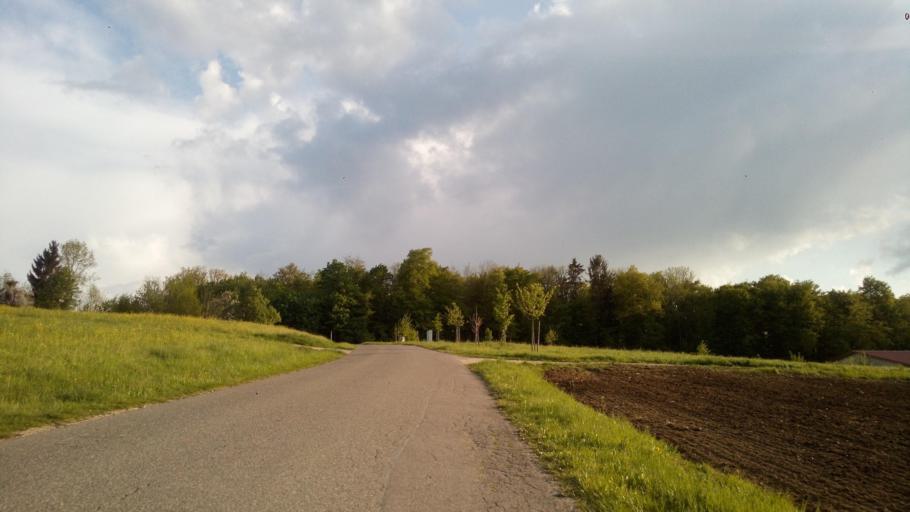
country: DE
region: Baden-Wuerttemberg
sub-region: Regierungsbezirk Stuttgart
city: Salach
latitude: 48.7023
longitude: 9.7512
